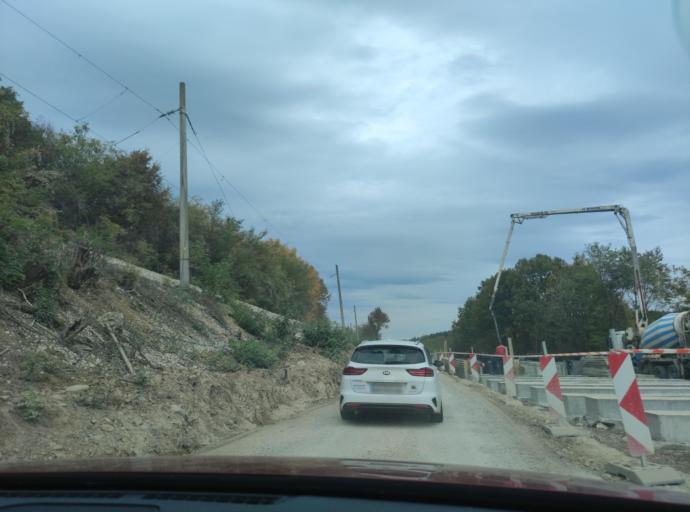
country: BG
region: Montana
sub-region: Obshtina Montana
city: Montana
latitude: 43.3835
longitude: 23.2429
